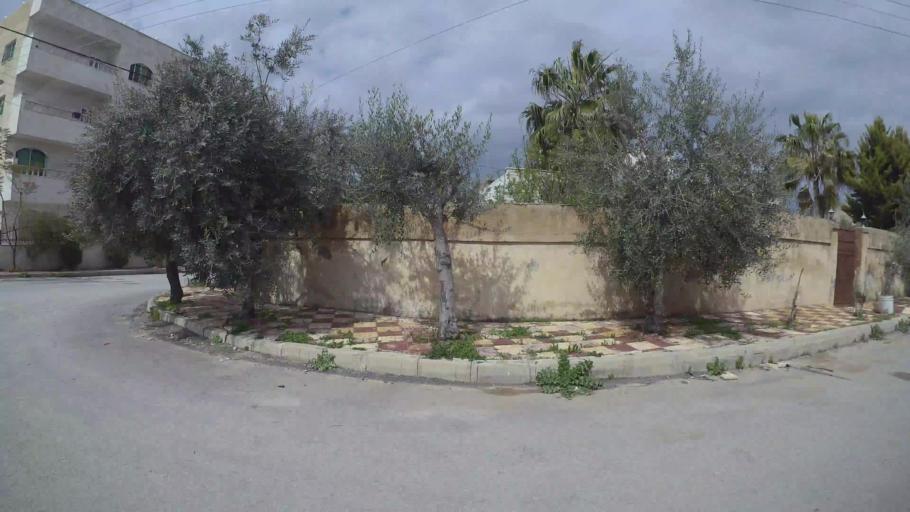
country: JO
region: Amman
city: Al Jubayhah
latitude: 32.0529
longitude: 35.8236
